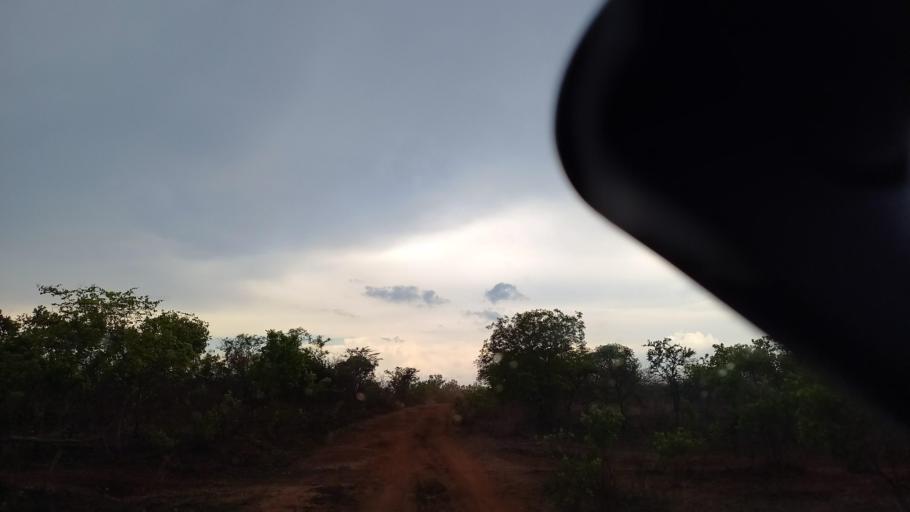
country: ZM
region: Lusaka
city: Kafue
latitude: -15.9963
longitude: 28.2765
